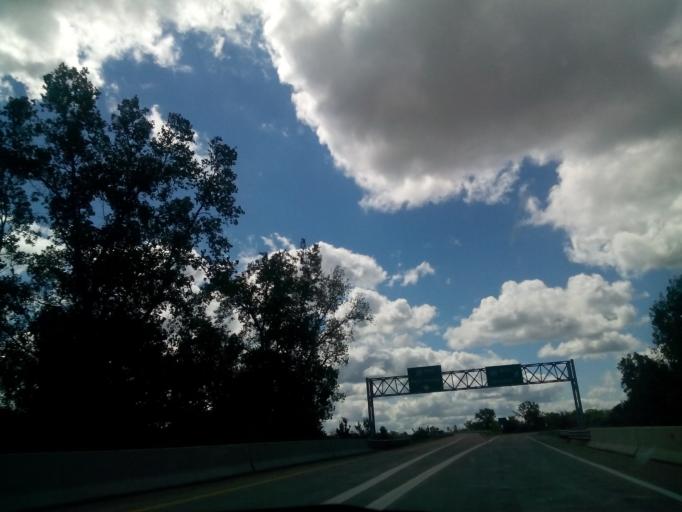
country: US
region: Michigan
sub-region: Genesee County
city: Flint
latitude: 42.9877
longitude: -83.7378
